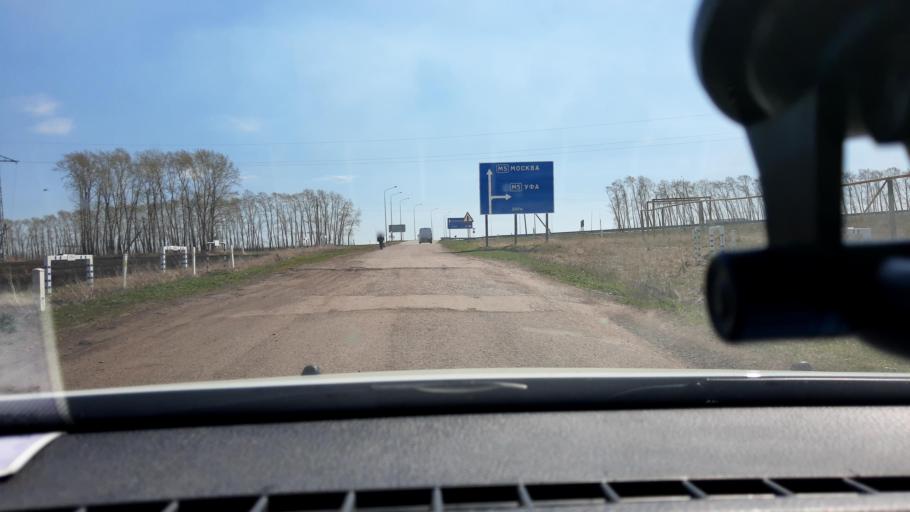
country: RU
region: Bashkortostan
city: Alekseyevka
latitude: 54.7274
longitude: 54.9234
